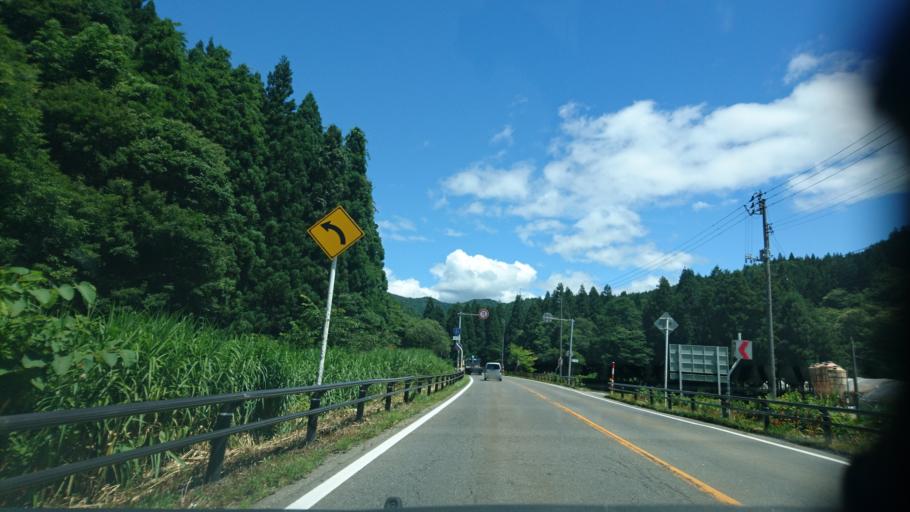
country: JP
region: Akita
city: Kakunodatemachi
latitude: 39.6540
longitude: 140.6720
